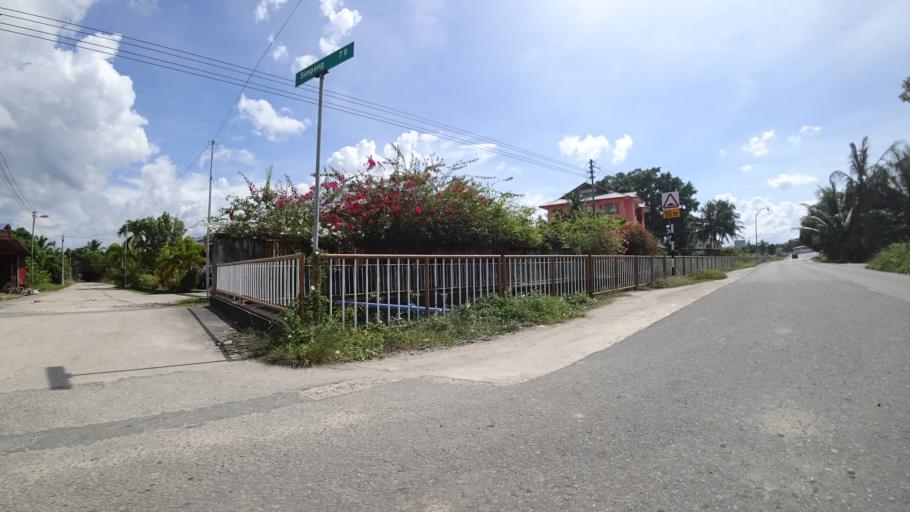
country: BN
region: Brunei and Muara
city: Bandar Seri Begawan
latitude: 4.8880
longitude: 114.8463
